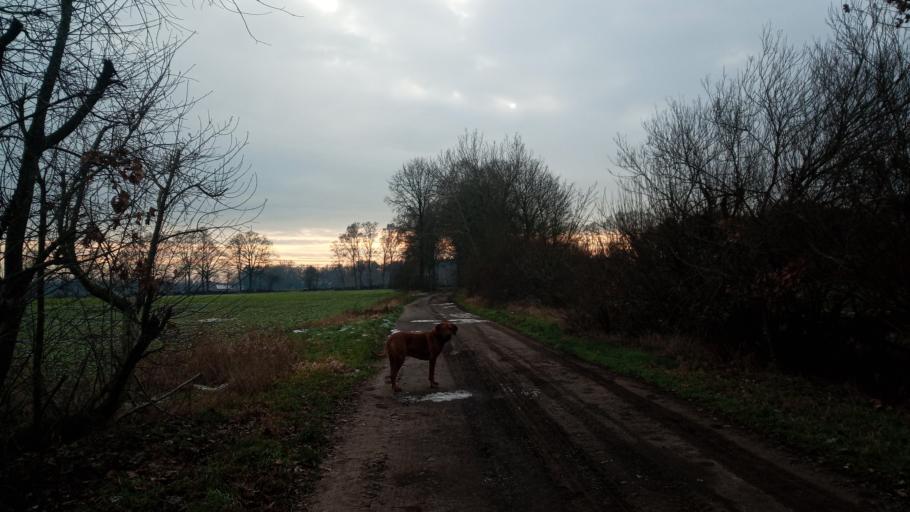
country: DE
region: Lower Saxony
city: Horstedt
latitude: 53.1619
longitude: 9.2494
